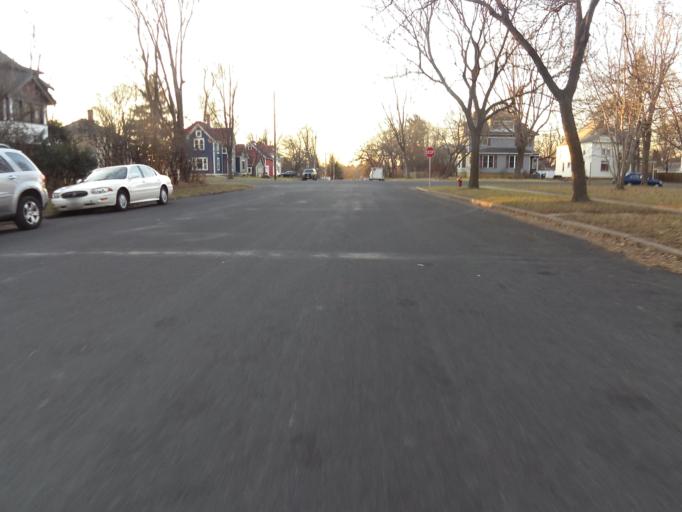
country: US
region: Wisconsin
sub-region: Pierce County
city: River Falls
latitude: 44.8594
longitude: -92.6201
